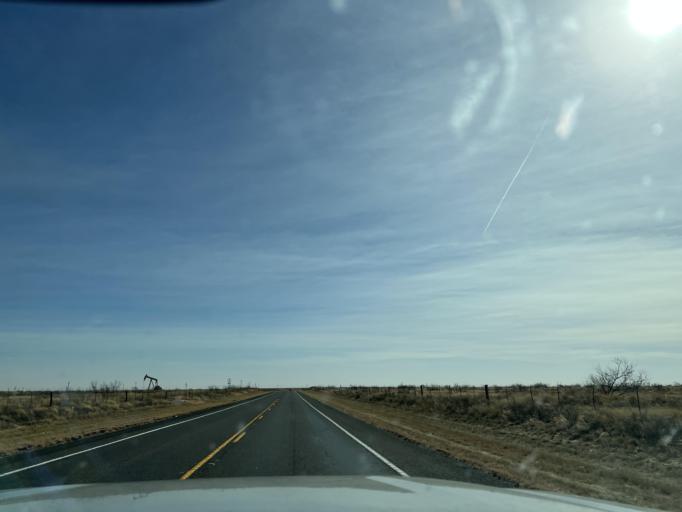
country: US
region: Texas
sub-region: Andrews County
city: Andrews
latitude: 32.4647
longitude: -102.4581
